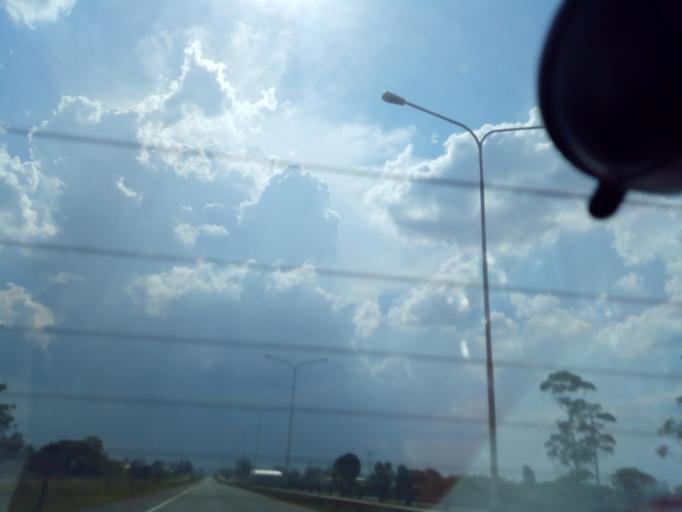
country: AR
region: Corrientes
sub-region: Departamento de Paso de los Libres
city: Paso de los Libres
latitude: -29.7220
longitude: -57.1536
